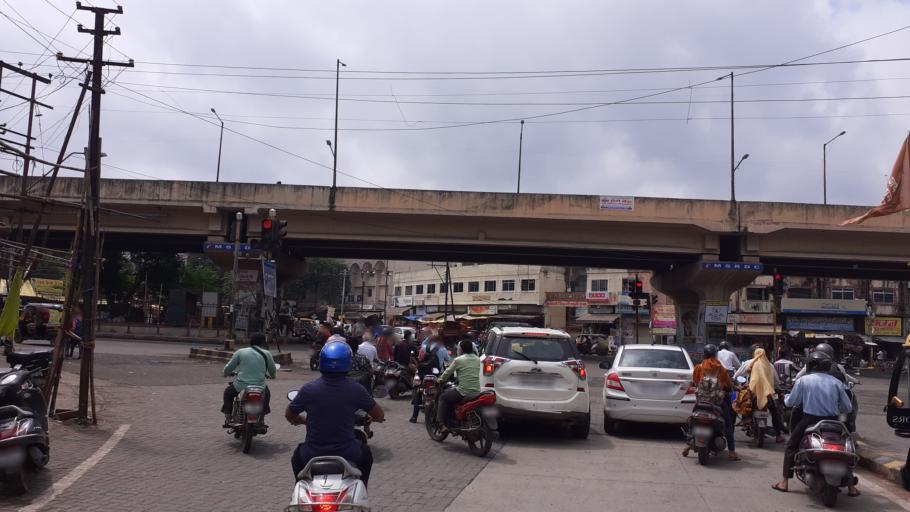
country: IN
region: Maharashtra
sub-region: Nagpur Division
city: Nagpur
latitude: 21.1287
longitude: 79.1135
